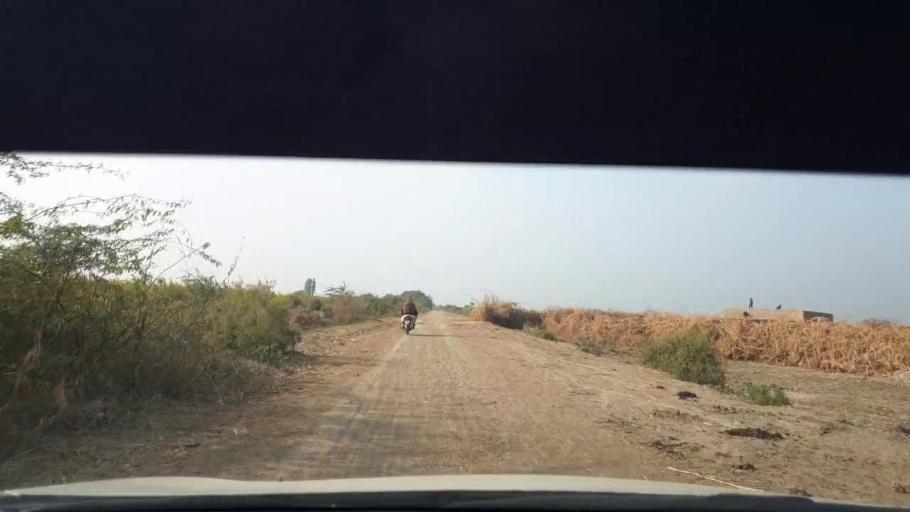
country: PK
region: Sindh
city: Berani
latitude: 25.7474
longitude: 68.9462
